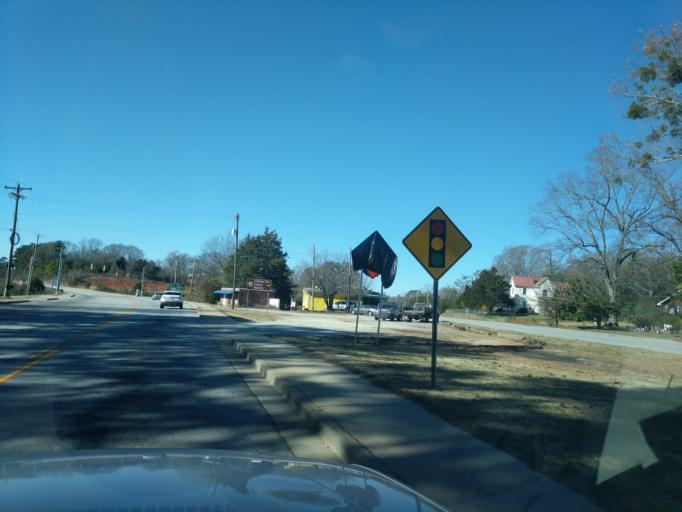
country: US
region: South Carolina
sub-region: Oconee County
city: Westminster
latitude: 34.6698
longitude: -83.1026
